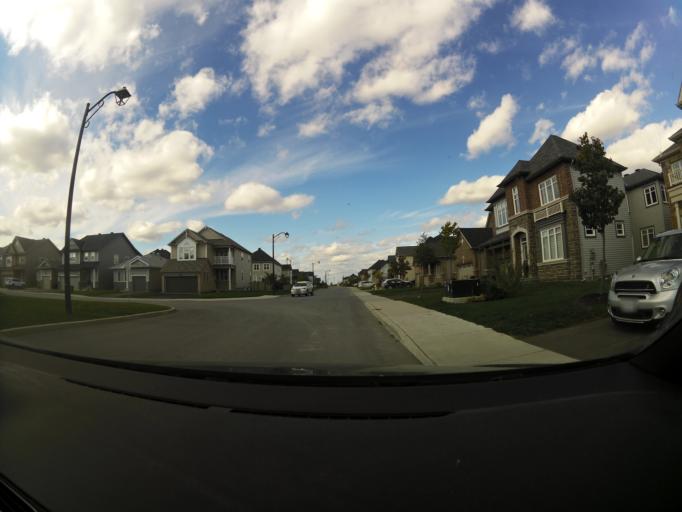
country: CA
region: Ontario
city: Bells Corners
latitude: 45.2728
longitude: -75.8868
